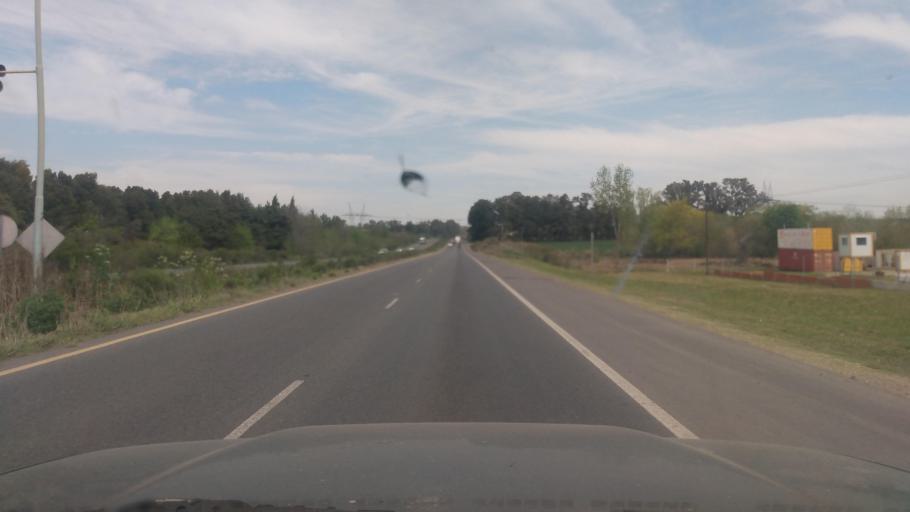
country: AR
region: Buenos Aires
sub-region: Partido de Lujan
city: Lujan
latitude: -34.4484
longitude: -59.0529
